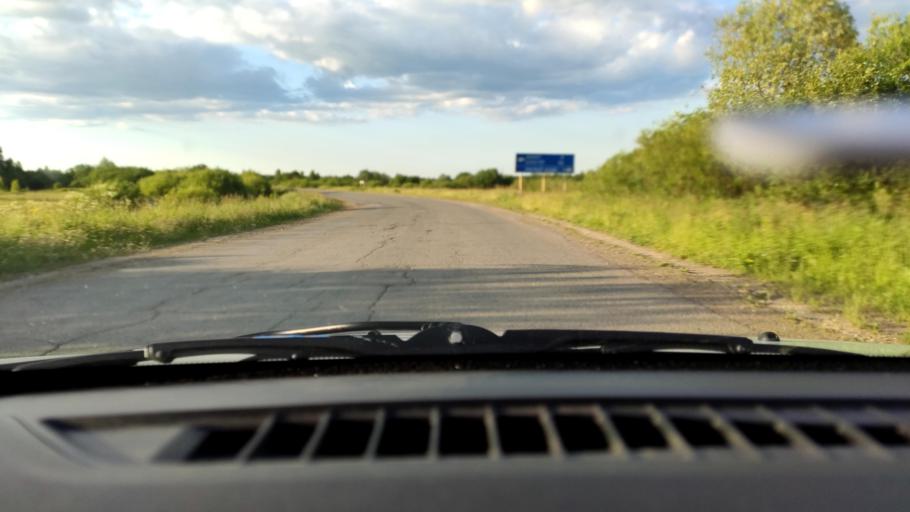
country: RU
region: Perm
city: Uinskoye
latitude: 57.0852
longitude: 56.5577
